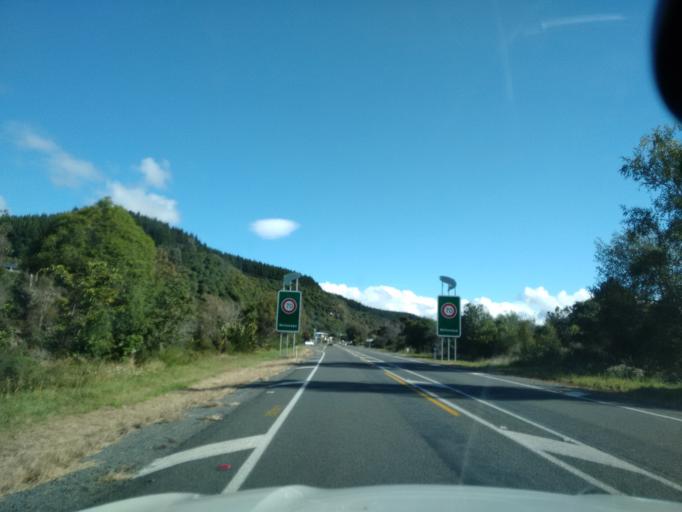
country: NZ
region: Waikato
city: Turangi
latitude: -38.9299
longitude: 175.8781
